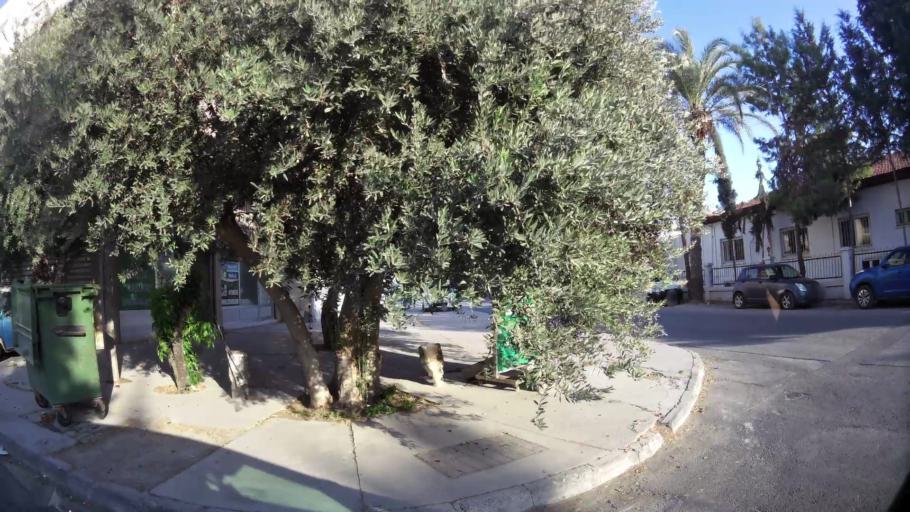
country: CY
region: Lefkosia
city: Nicosia
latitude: 35.1854
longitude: 33.3636
